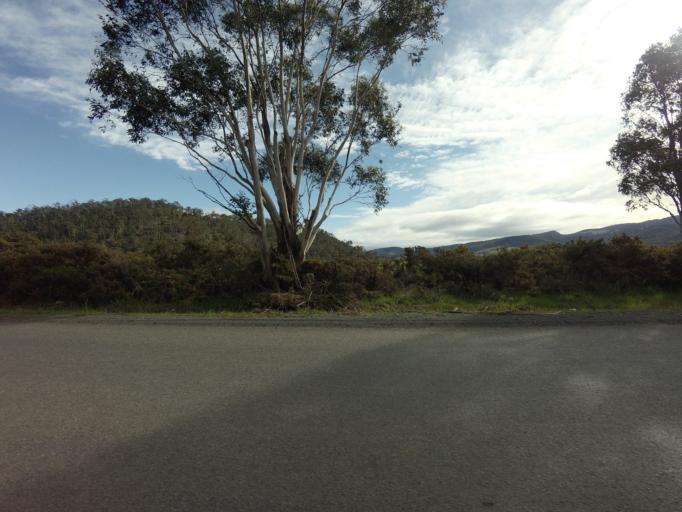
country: AU
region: Tasmania
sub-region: Derwent Valley
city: New Norfolk
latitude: -42.7788
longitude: 147.0173
